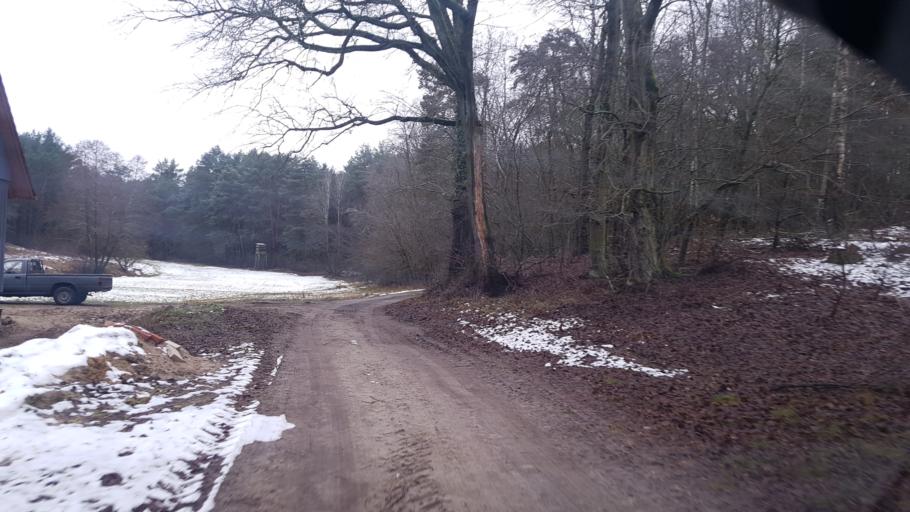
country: DE
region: Brandenburg
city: Jamlitz
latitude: 51.9969
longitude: 14.3584
